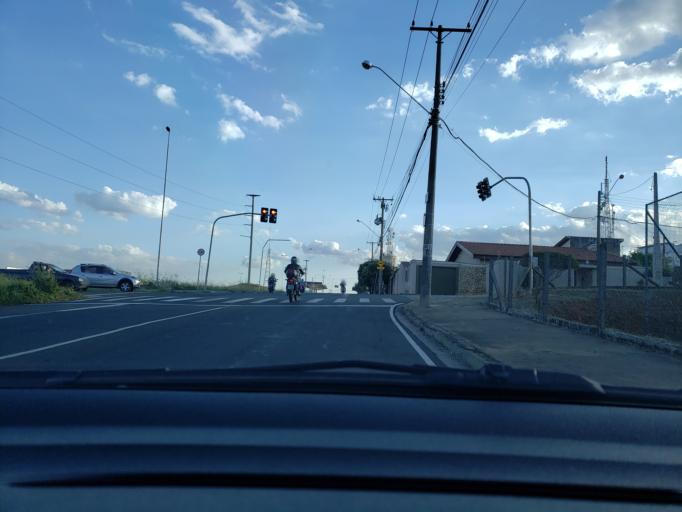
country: BR
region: Sao Paulo
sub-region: Americana
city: Americana
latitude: -22.7320
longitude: -47.3511
